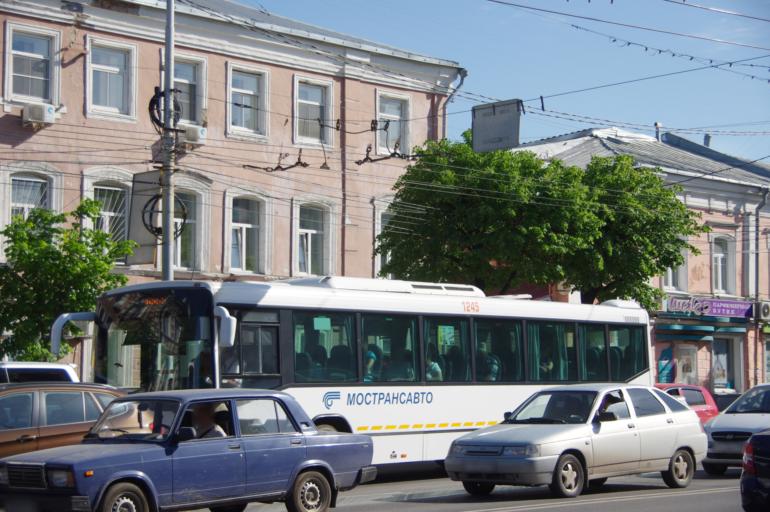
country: RU
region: Rjazan
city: Ryazan'
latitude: 54.6314
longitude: 39.7398
